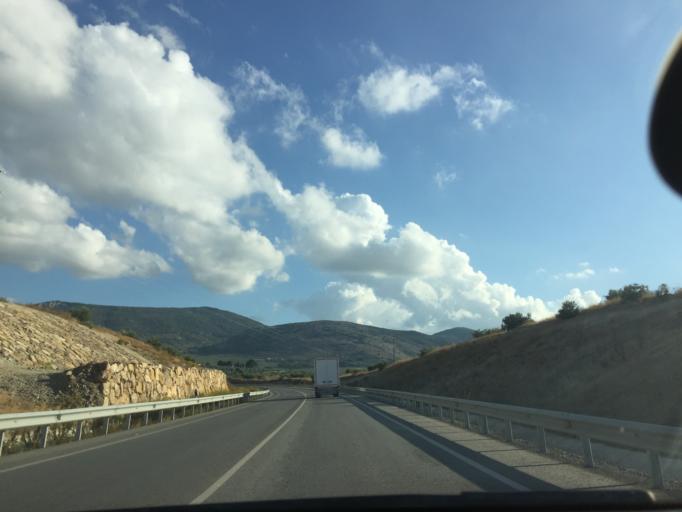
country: ES
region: Andalusia
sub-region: Provincia de Jaen
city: Mancha Real
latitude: 37.8005
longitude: -3.6247
